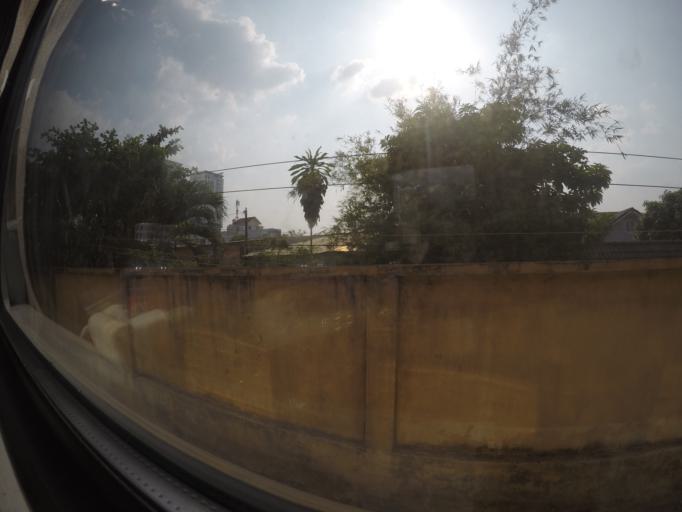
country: VN
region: Dong Nai
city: Bien Hoa
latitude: 10.9492
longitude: 106.8264
